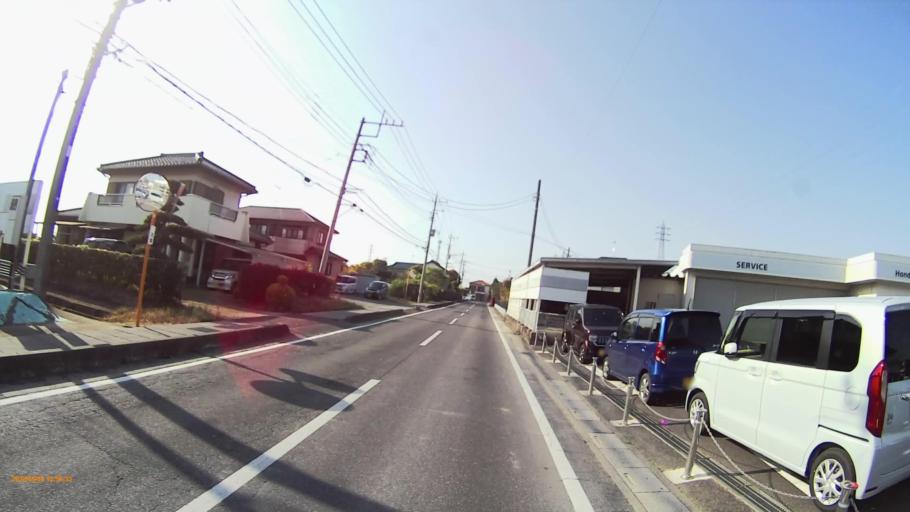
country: JP
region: Saitama
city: Satte
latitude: 36.0581
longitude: 139.7144
